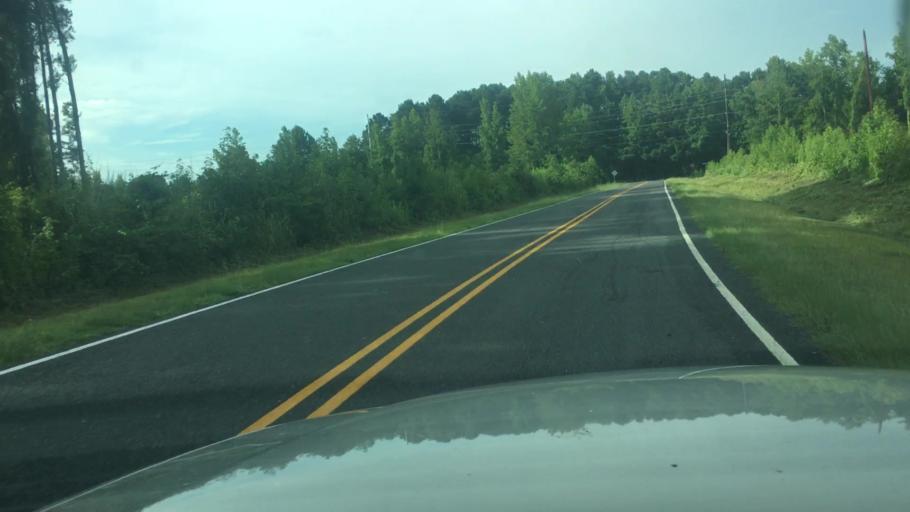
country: US
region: North Carolina
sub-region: Cumberland County
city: Eastover
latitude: 35.1624
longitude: -78.8539
